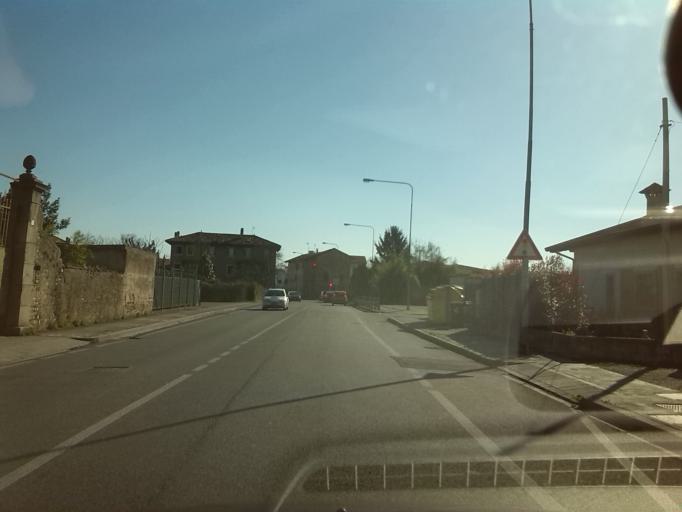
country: IT
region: Friuli Venezia Giulia
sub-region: Provincia di Udine
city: Udine
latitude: 46.0723
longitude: 13.2626
